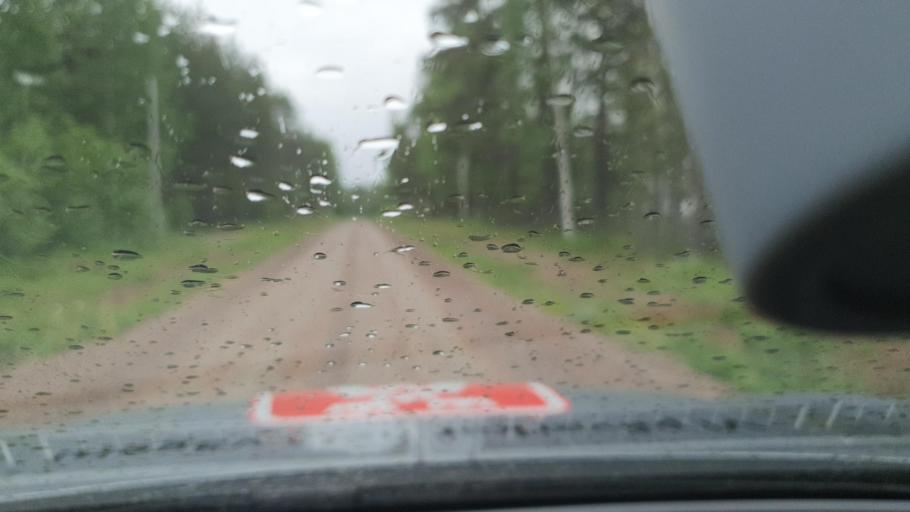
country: SE
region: Norrbotten
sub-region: Overkalix Kommun
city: OEverkalix
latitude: 66.4994
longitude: 22.7603
